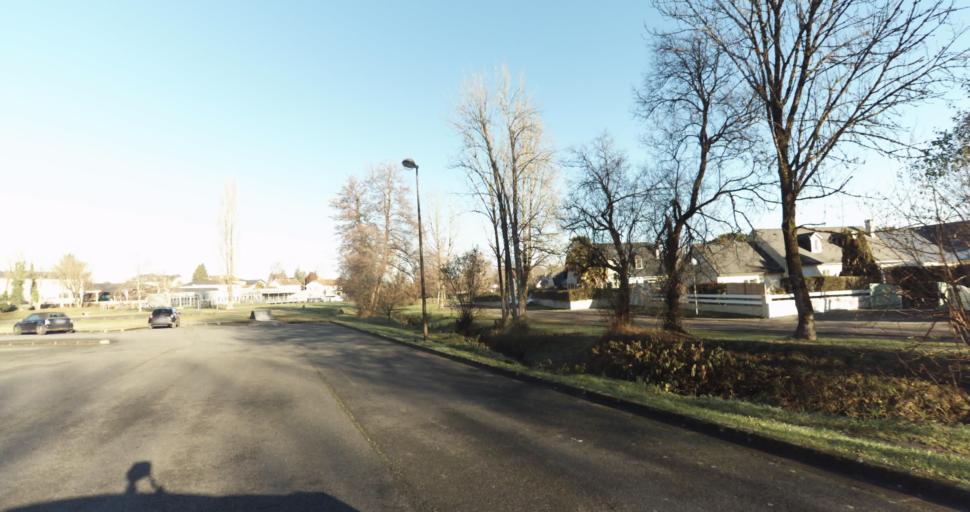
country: FR
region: Aquitaine
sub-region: Departement des Pyrenees-Atlantiques
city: Morlaas
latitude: 43.3442
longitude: -0.2601
